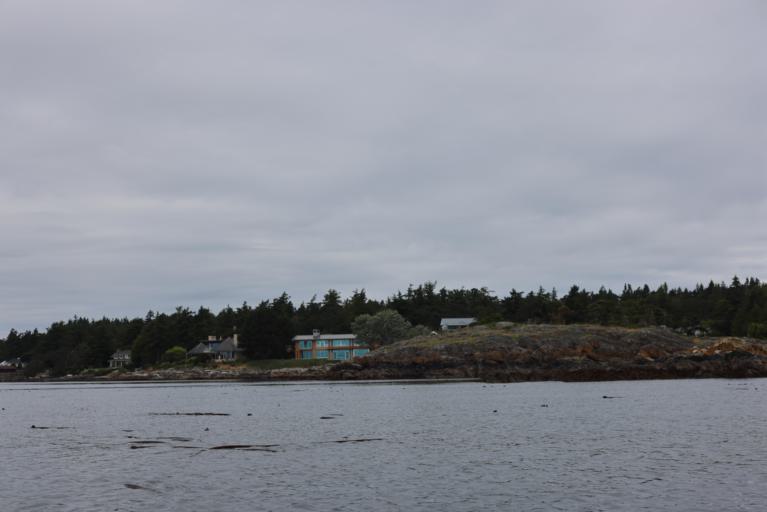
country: CA
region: British Columbia
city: Oak Bay
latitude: 48.4474
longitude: -123.2793
